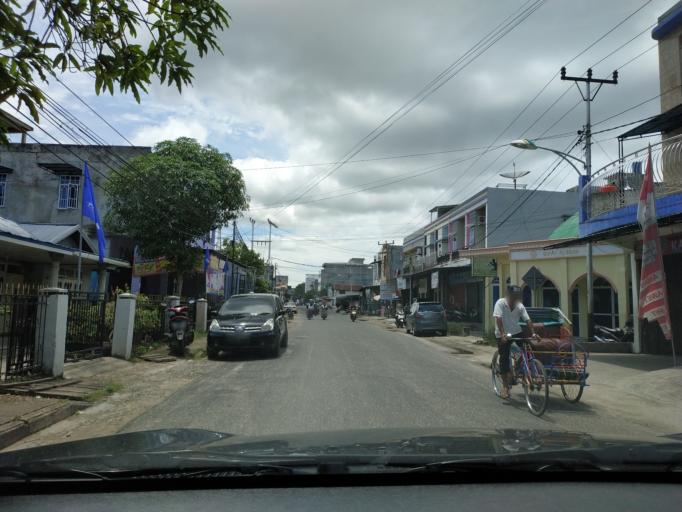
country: ID
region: Riau
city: Tembilahan
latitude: -0.3220
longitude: 103.1608
